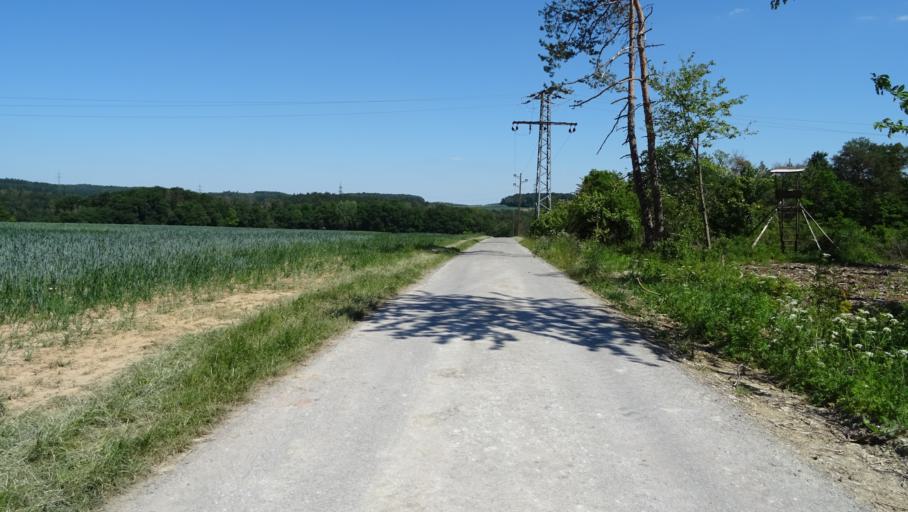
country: DE
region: Baden-Wuerttemberg
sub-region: Karlsruhe Region
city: Buchen
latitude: 49.4906
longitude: 9.3293
